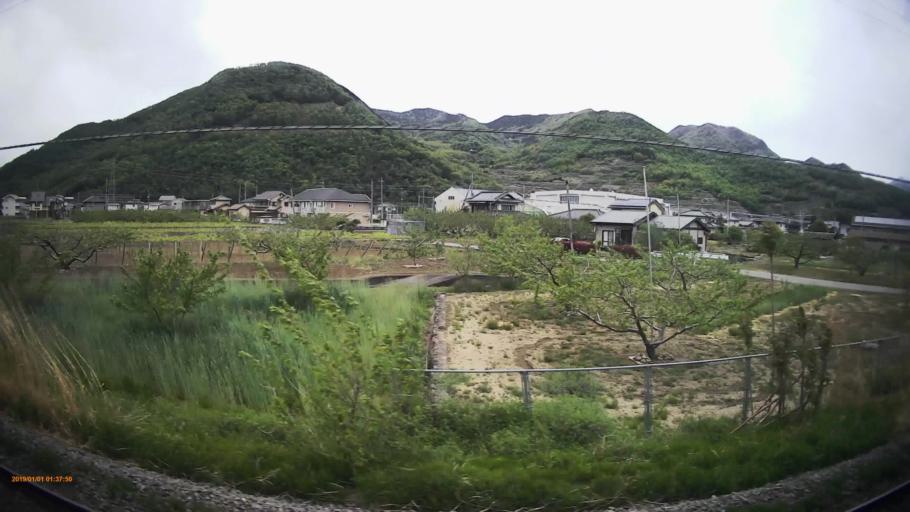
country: JP
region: Yamanashi
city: Isawa
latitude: 35.6622
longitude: 138.6447
